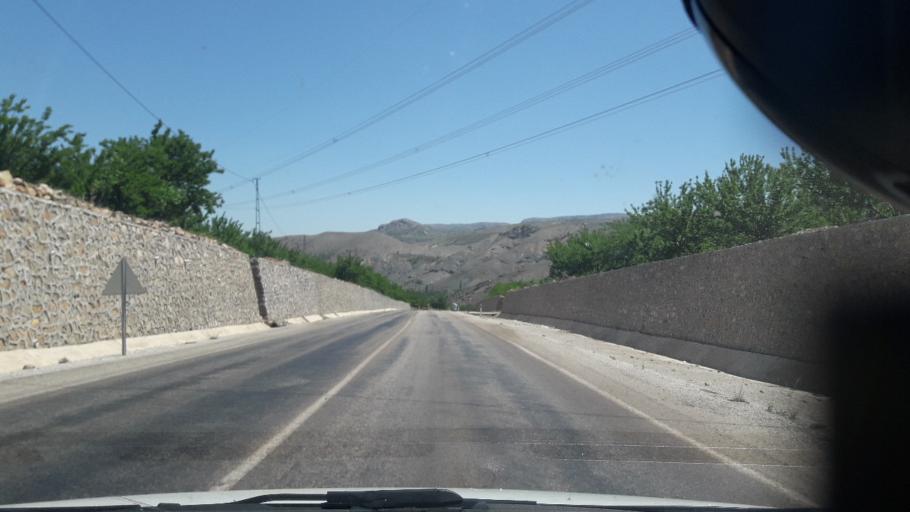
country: TR
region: Malatya
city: Hekimhan
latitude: 38.8381
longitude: 37.8443
